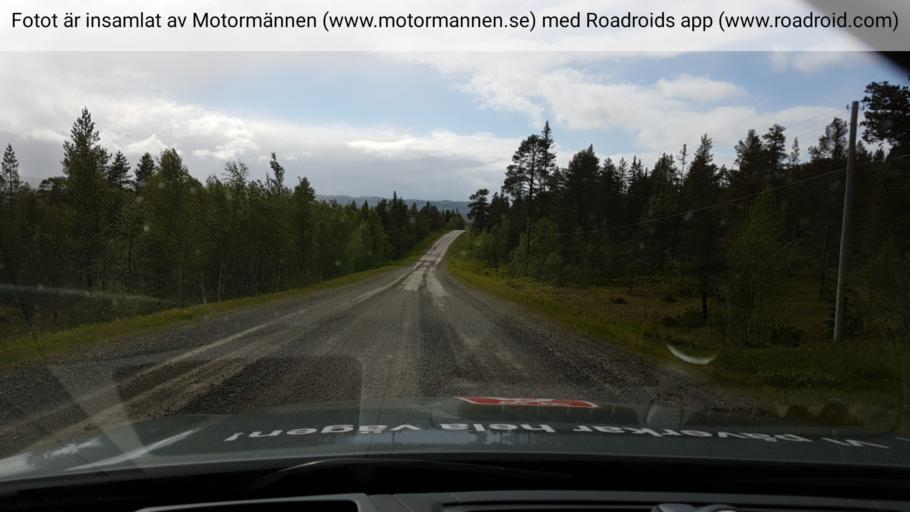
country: NO
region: Nord-Trondelag
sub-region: Snasa
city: Snaase
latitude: 63.7330
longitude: 12.5161
